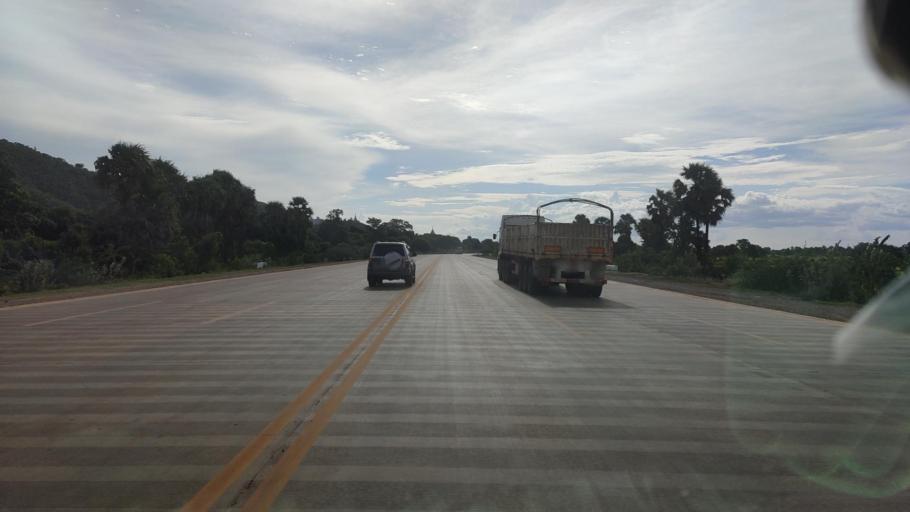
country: MM
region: Mandalay
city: Kyaukse
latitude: 21.6104
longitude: 96.1641
